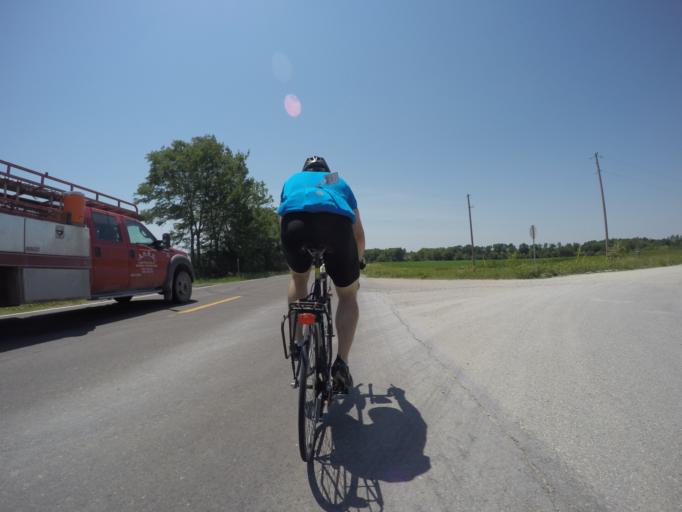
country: US
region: Nebraska
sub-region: Pawnee County
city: Pawnee City
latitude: 40.0299
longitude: -96.0482
